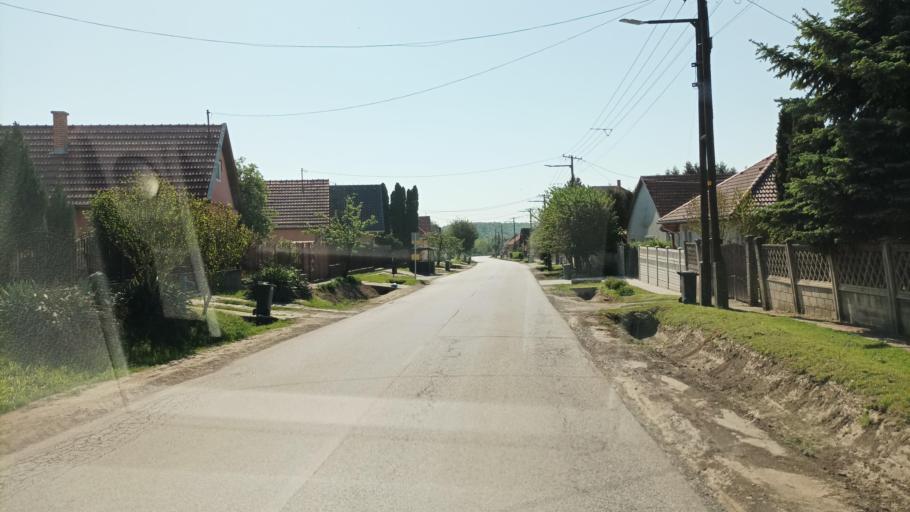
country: HU
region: Pest
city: Gomba
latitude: 47.3593
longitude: 19.5344
